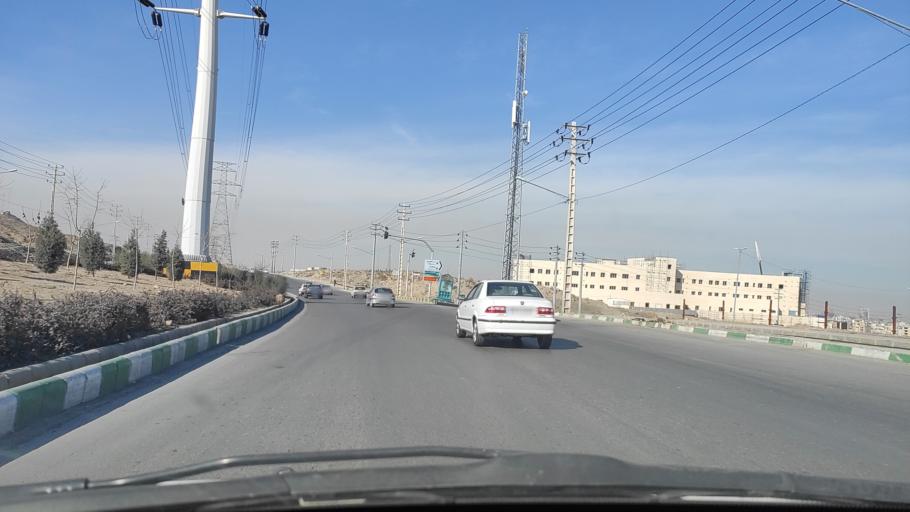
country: IR
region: Razavi Khorasan
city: Mashhad
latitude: 36.2746
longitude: 59.5379
